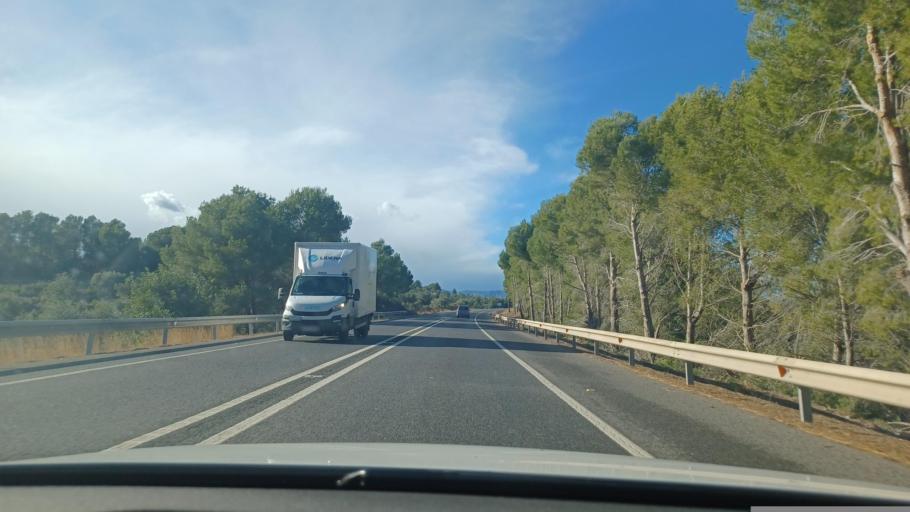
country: ES
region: Catalonia
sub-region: Provincia de Tarragona
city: l'Ametlla de Mar
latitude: 40.8949
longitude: 0.7614
